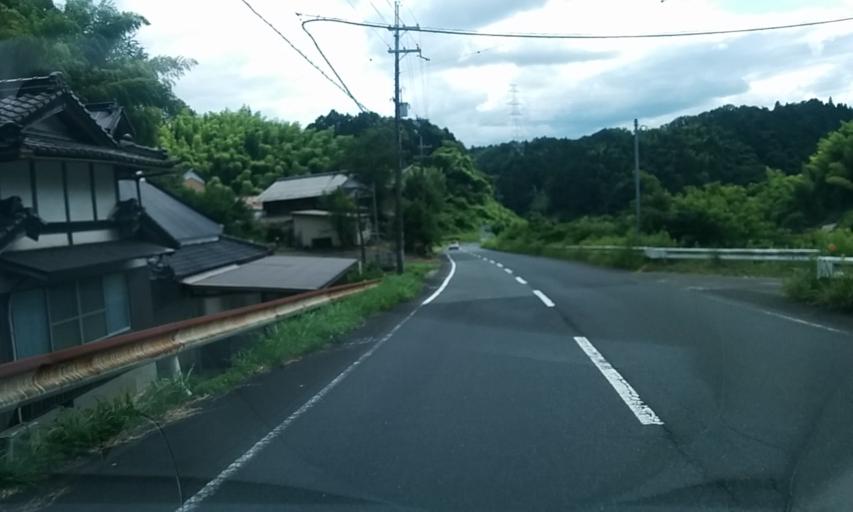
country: JP
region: Kyoto
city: Ayabe
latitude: 35.3473
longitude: 135.2735
